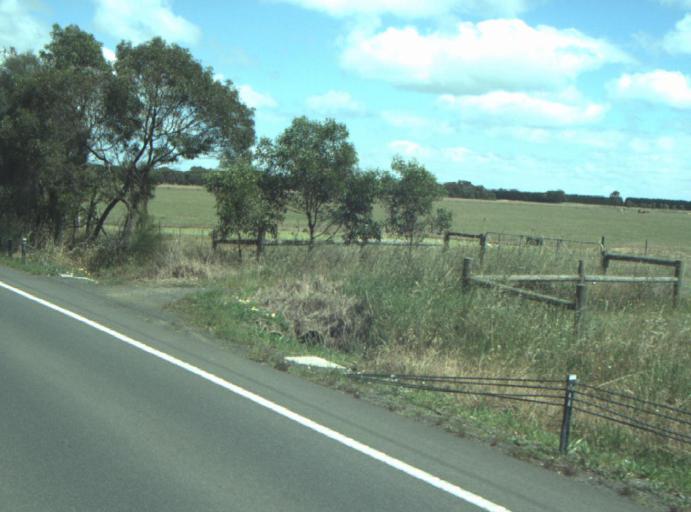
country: AU
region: Victoria
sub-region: Queenscliffe
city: Queenscliff
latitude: -38.1852
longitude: 144.6711
